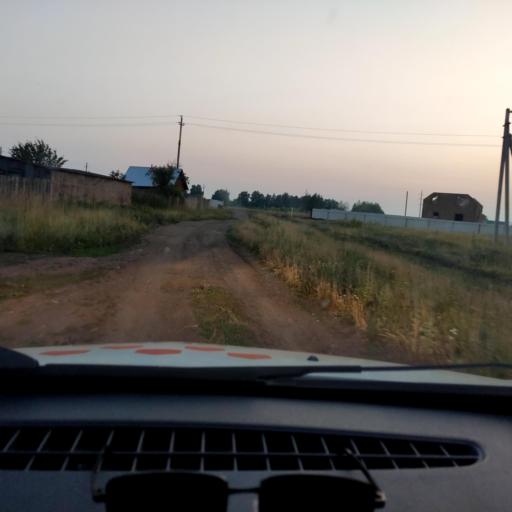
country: RU
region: Bashkortostan
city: Ulukulevo
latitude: 54.3693
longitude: 56.4295
